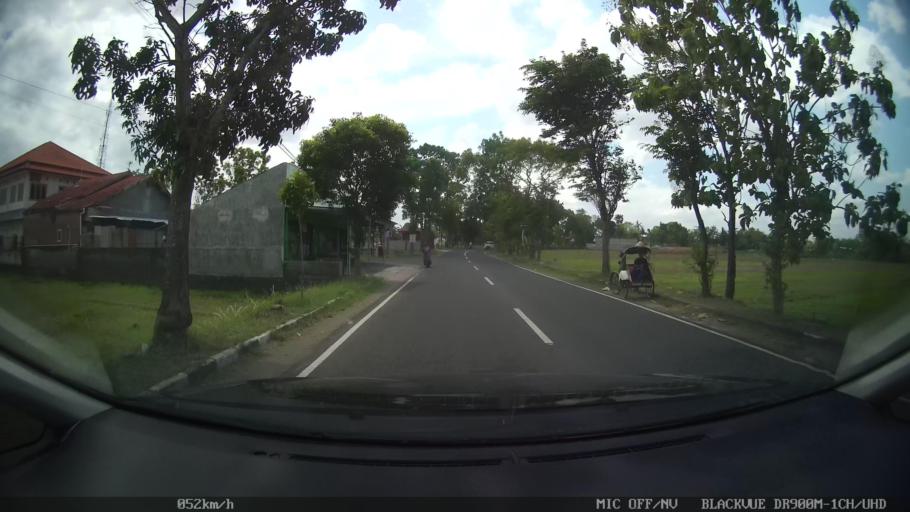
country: ID
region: Daerah Istimewa Yogyakarta
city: Bantul
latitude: -7.8879
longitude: 110.3338
